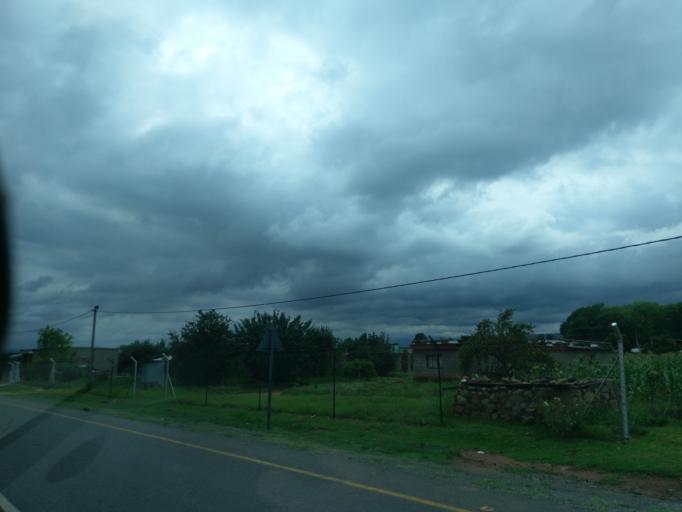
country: LS
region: Maseru
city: Maseru
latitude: -29.4858
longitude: 27.5251
